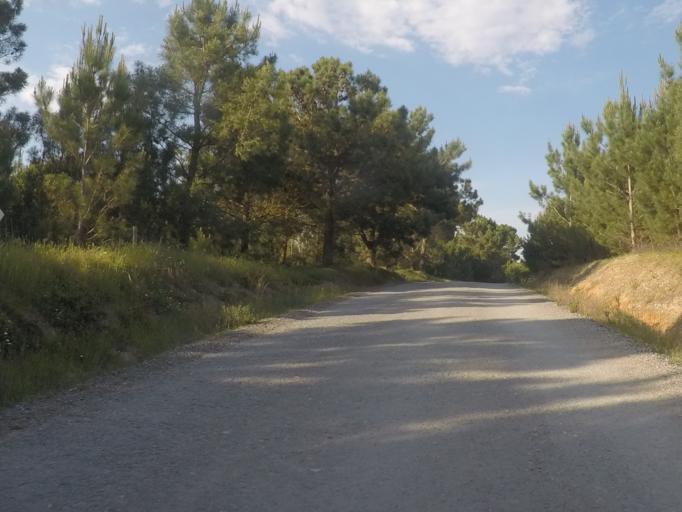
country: PT
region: Setubal
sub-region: Sesimbra
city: Sesimbra
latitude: 38.4586
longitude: -9.1866
